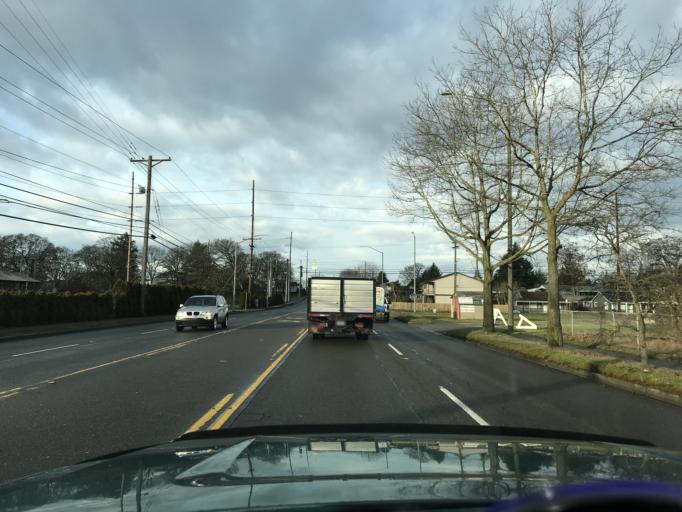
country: US
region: Washington
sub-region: Pierce County
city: Lakewood
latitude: 47.1906
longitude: -122.4917
